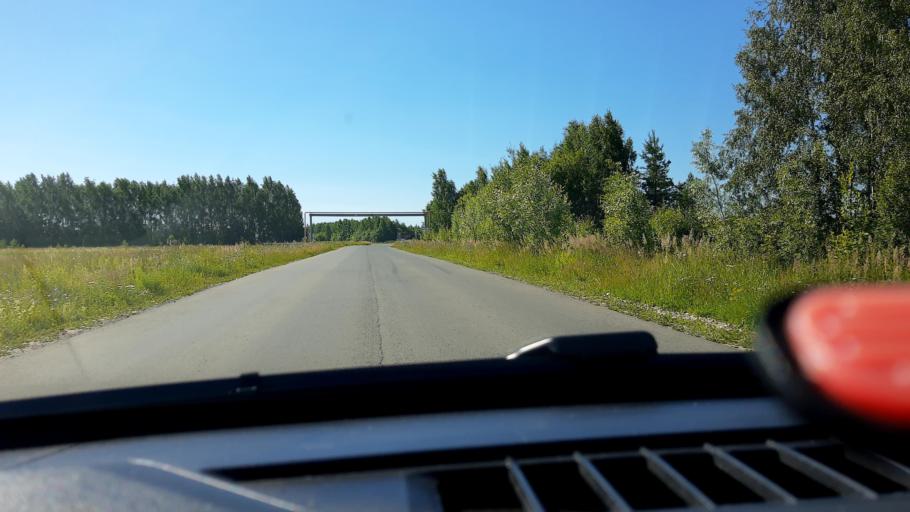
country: RU
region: Nizjnij Novgorod
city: Babino
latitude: 56.1362
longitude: 43.6428
